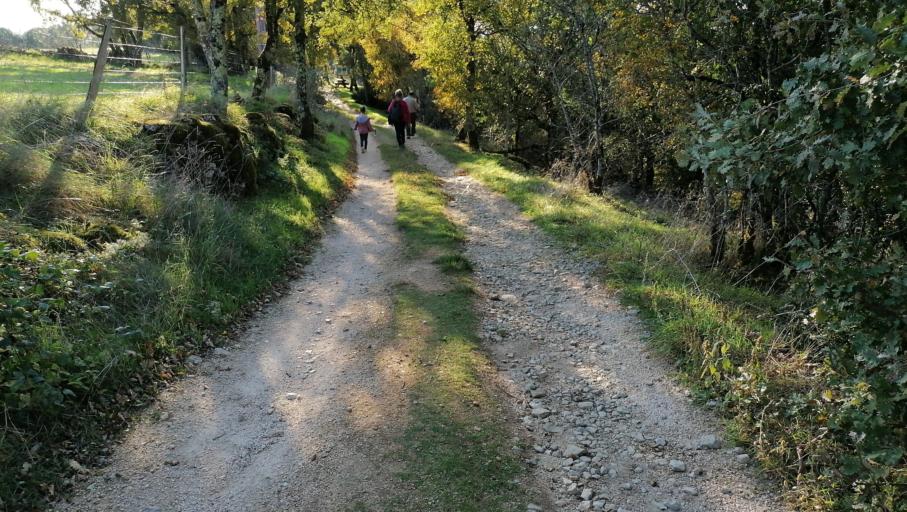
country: FR
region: Midi-Pyrenees
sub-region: Departement du Lot
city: Vayrac
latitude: 44.8984
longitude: 1.6554
